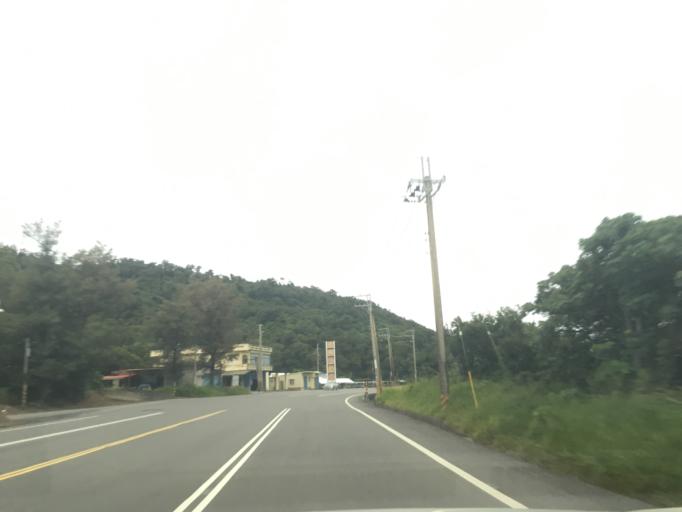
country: TW
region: Taiwan
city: Hengchun
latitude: 22.3297
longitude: 120.8923
